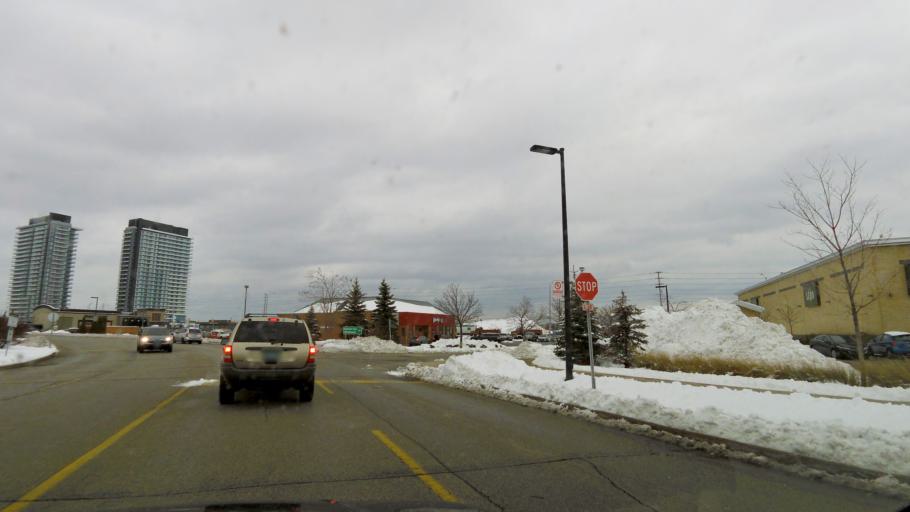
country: CA
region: Ontario
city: Mississauga
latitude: 43.5559
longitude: -79.7119
